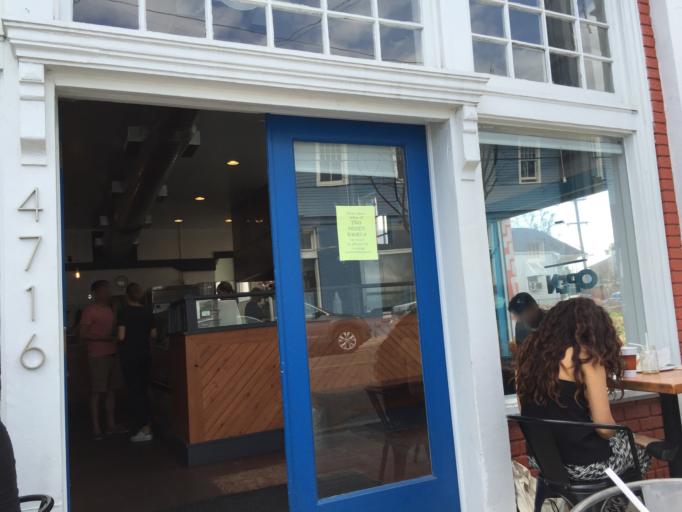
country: US
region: Louisiana
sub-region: Jefferson Parish
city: Marrero
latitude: 29.9349
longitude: -90.1069
